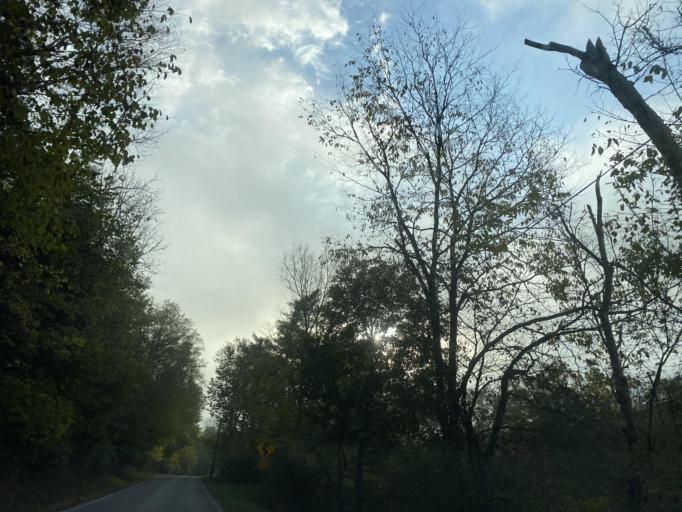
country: US
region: Kentucky
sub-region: Pendleton County
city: Falmouth
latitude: 38.7253
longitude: -84.3139
